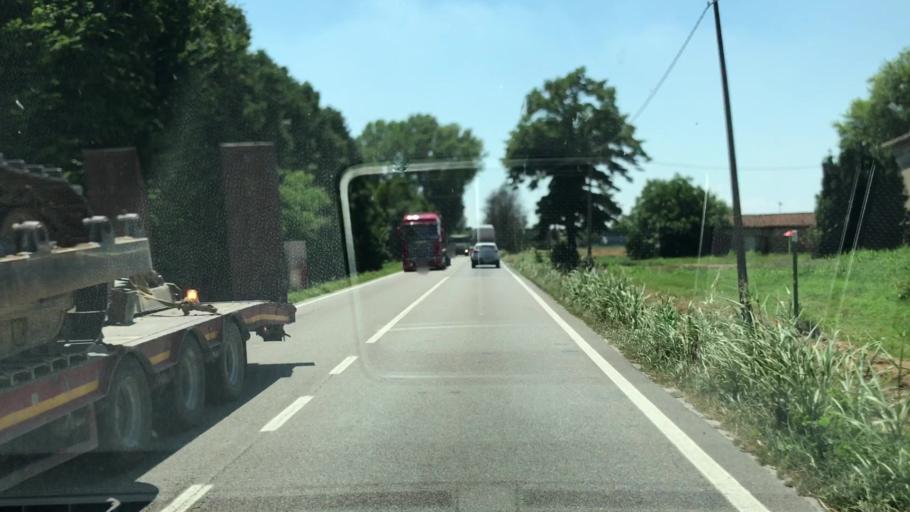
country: IT
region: Lombardy
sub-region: Provincia di Mantova
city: Pegognaga
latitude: 44.9936
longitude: 10.8746
